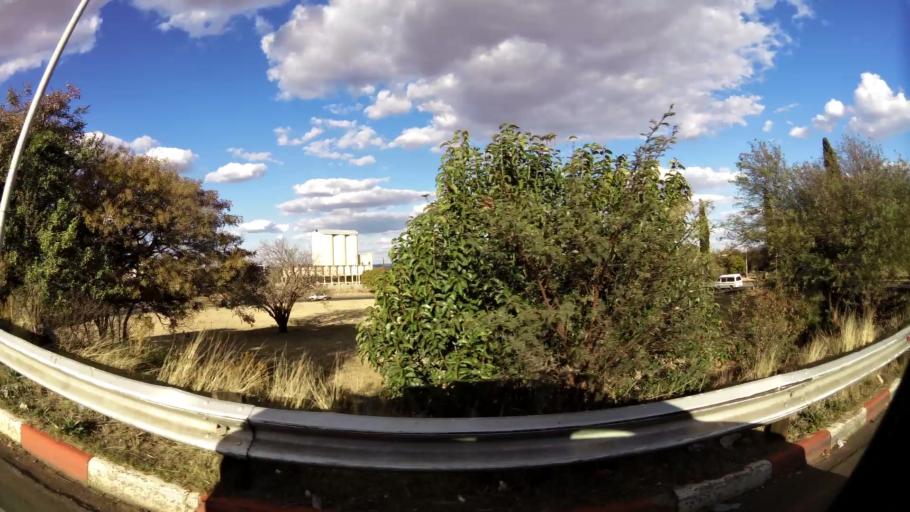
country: ZA
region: North-West
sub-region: Dr Kenneth Kaunda District Municipality
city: Potchefstroom
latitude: -26.7164
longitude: 27.0856
